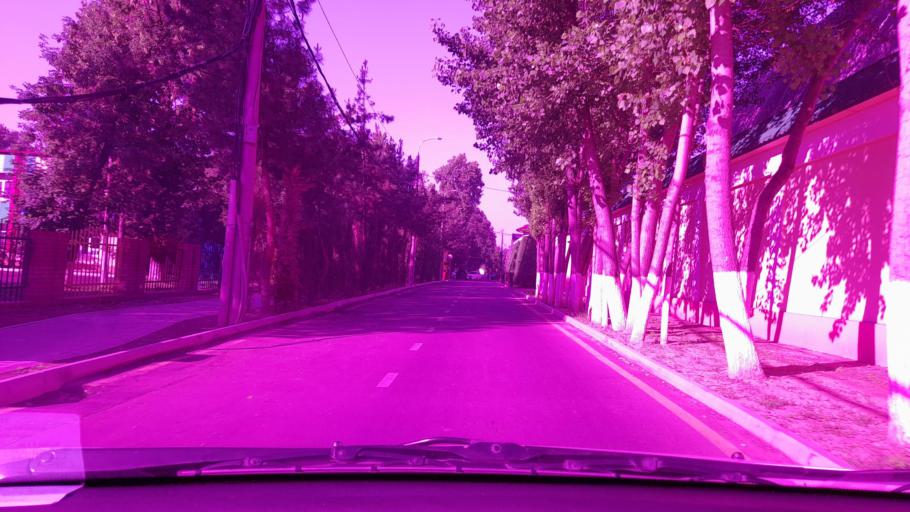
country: UZ
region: Toshkent
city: Salor
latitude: 41.3312
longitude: 69.3610
